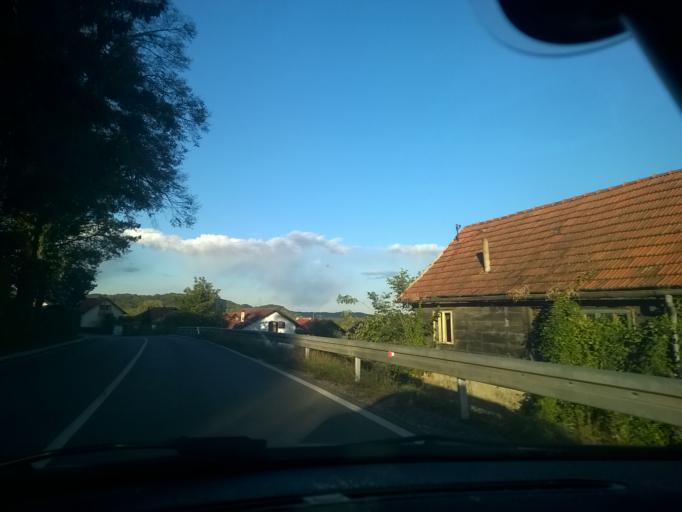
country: HR
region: Zagrebacka
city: Jakovlje
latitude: 46.0056
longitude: 15.8510
